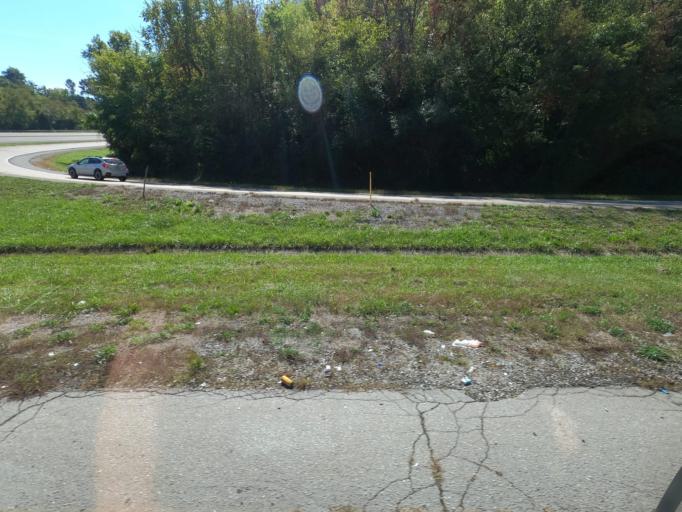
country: US
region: Tennessee
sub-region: Hamblen County
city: Morristown
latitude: 36.1939
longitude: -83.2670
